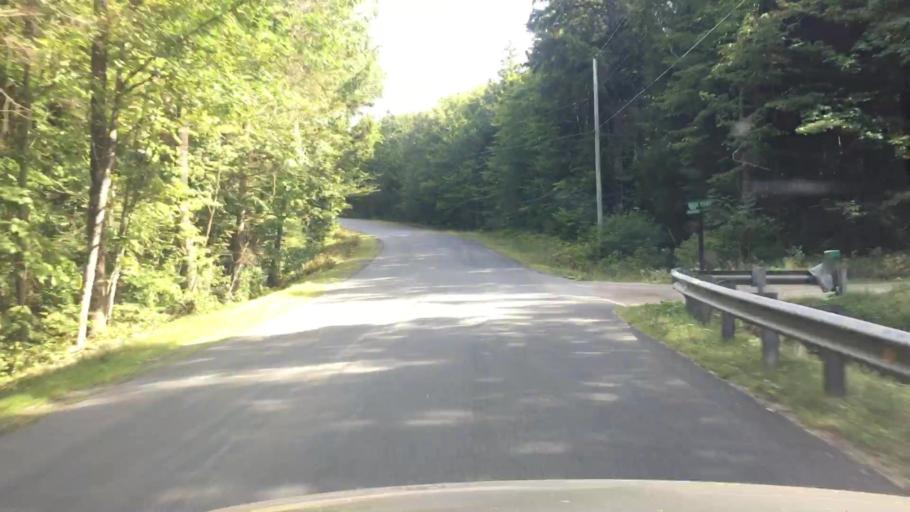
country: US
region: Vermont
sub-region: Windham County
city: Dover
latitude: 42.8427
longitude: -72.8291
